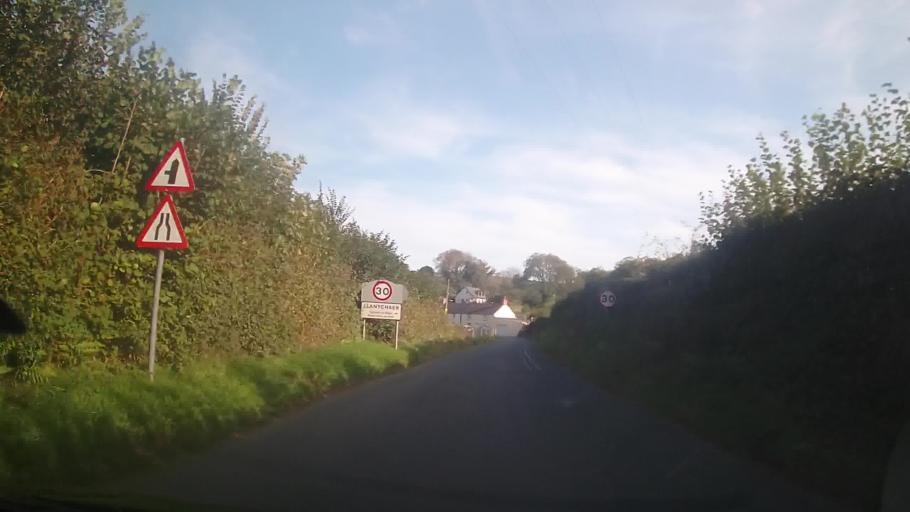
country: GB
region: Wales
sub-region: Pembrokeshire
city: Fishguard
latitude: 51.9812
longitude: -4.9339
